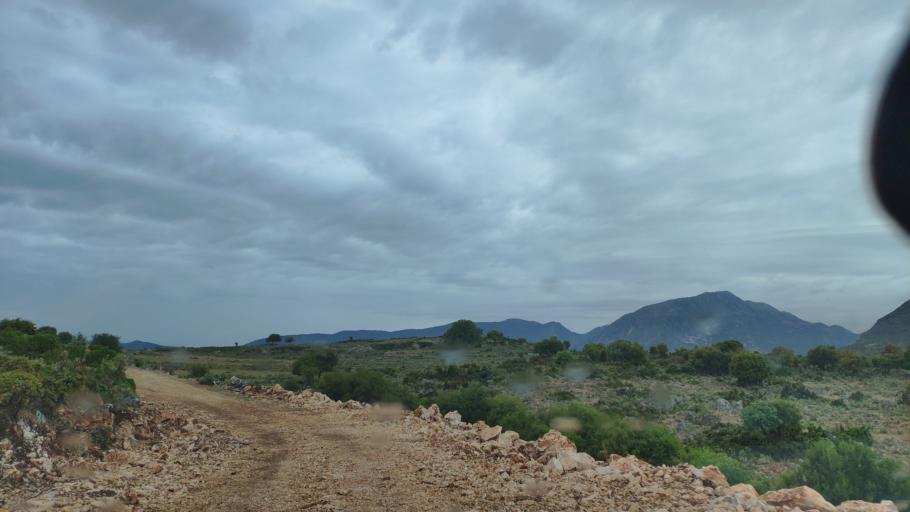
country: GR
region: West Greece
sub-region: Nomos Aitolias kai Akarnanias
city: Archontochorion
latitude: 38.6830
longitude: 21.0237
